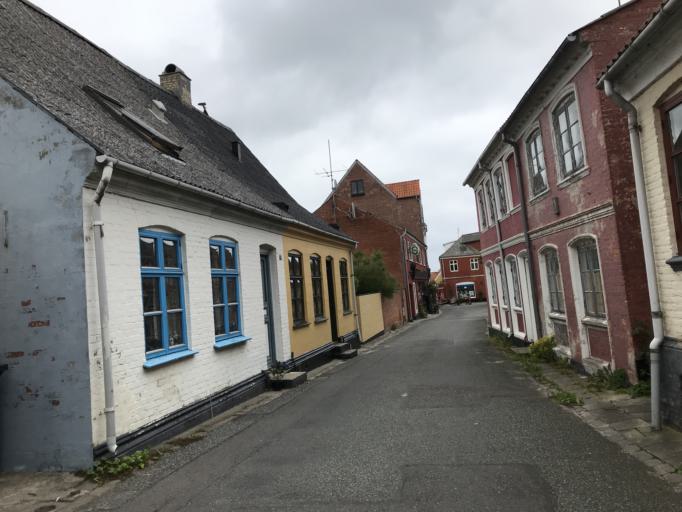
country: DK
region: South Denmark
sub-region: AEro Kommune
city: Marstal
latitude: 54.8537
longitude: 10.5171
